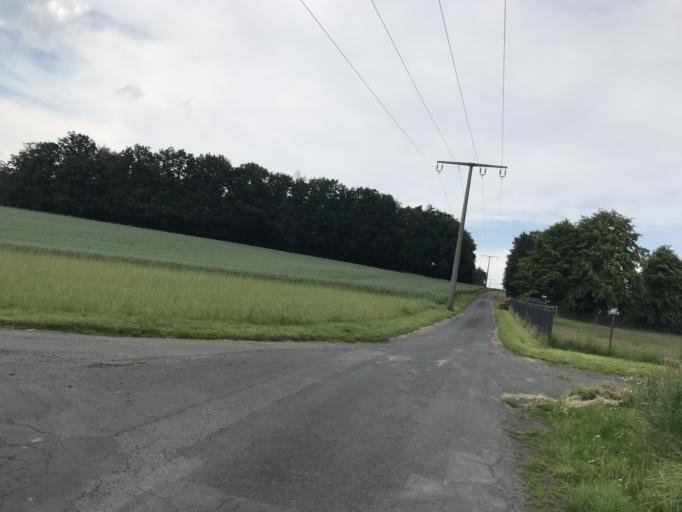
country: DE
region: Hesse
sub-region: Regierungsbezirk Giessen
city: Laubach
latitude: 50.5279
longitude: 8.9699
